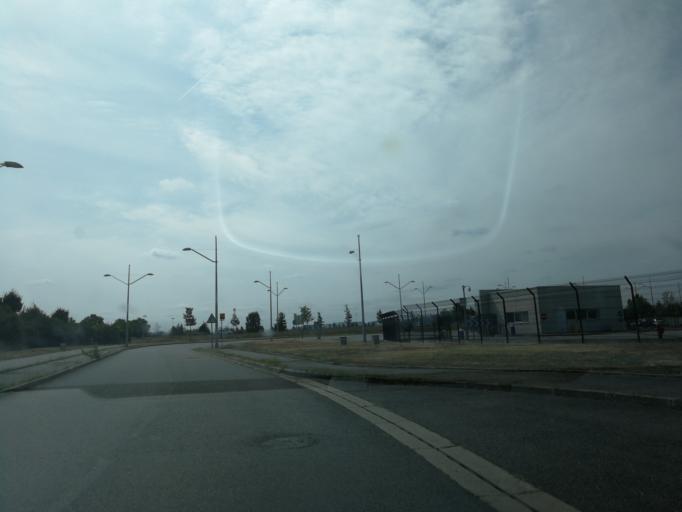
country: FR
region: Midi-Pyrenees
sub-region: Departement de la Haute-Garonne
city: Beauzelle
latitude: 43.6463
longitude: 1.3645
